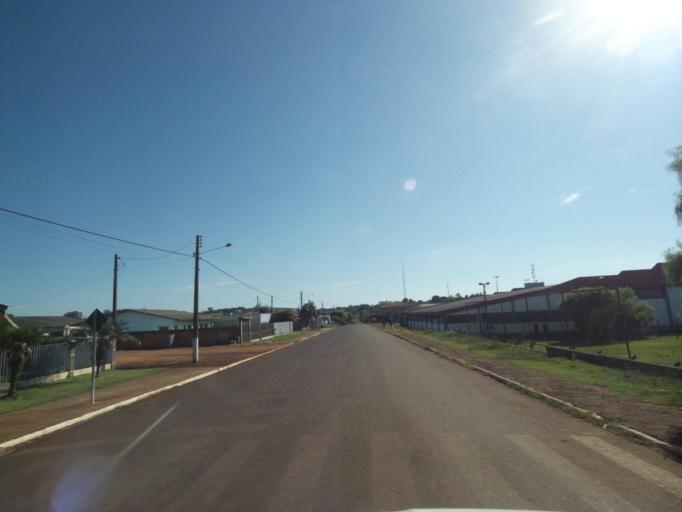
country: BR
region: Parana
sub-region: Laranjeiras Do Sul
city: Laranjeiras do Sul
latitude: -25.4927
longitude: -52.5318
